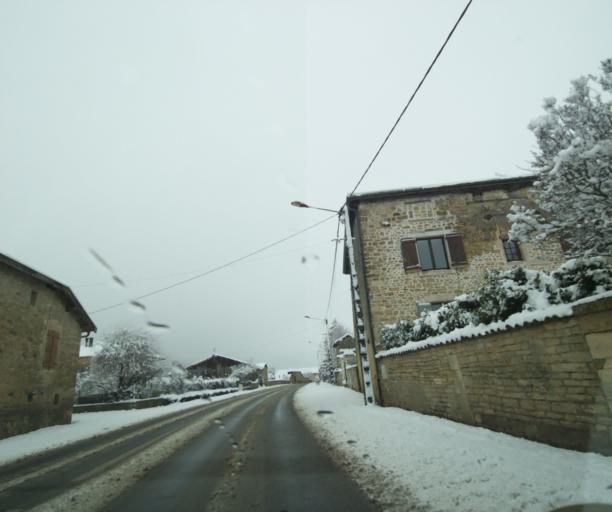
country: FR
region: Champagne-Ardenne
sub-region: Departement de la Haute-Marne
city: Wassy
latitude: 48.5240
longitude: 4.9306
